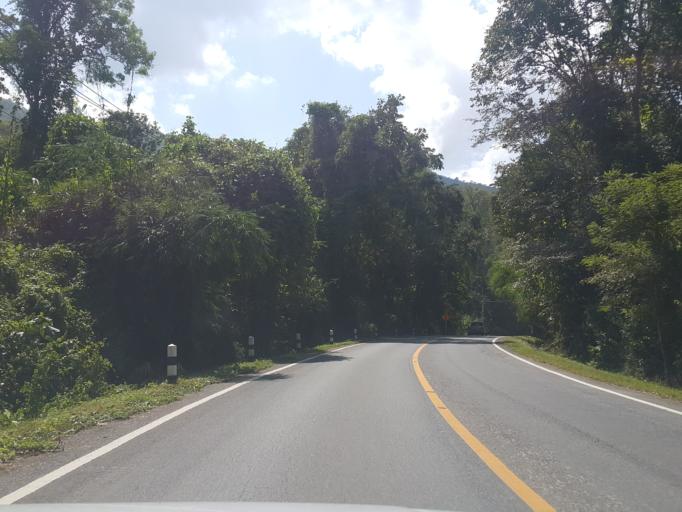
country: TH
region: Chiang Mai
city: Chom Thong
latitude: 18.5282
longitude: 98.6218
